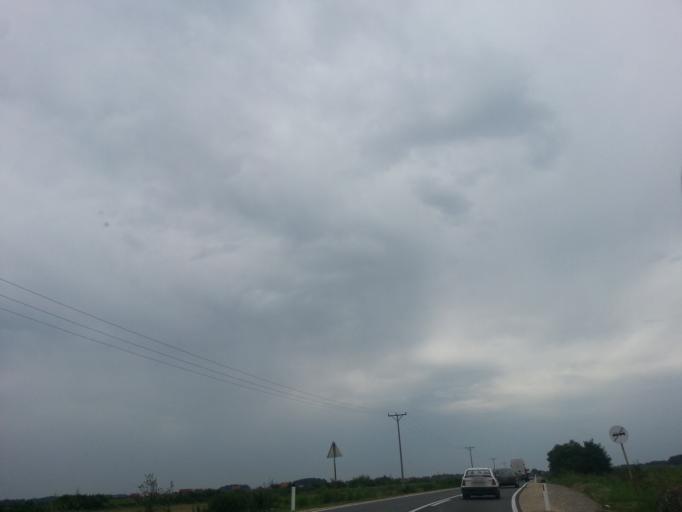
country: HR
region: Vukovarsko-Srijemska
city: Soljani
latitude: 44.8412
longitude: 18.9701
